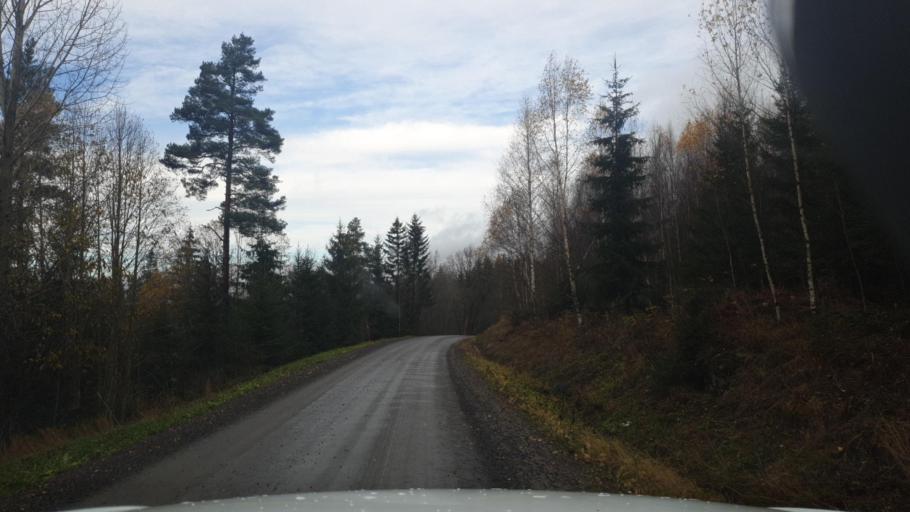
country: NO
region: Ostfold
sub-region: Romskog
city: Romskog
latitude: 59.8354
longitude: 11.9832
